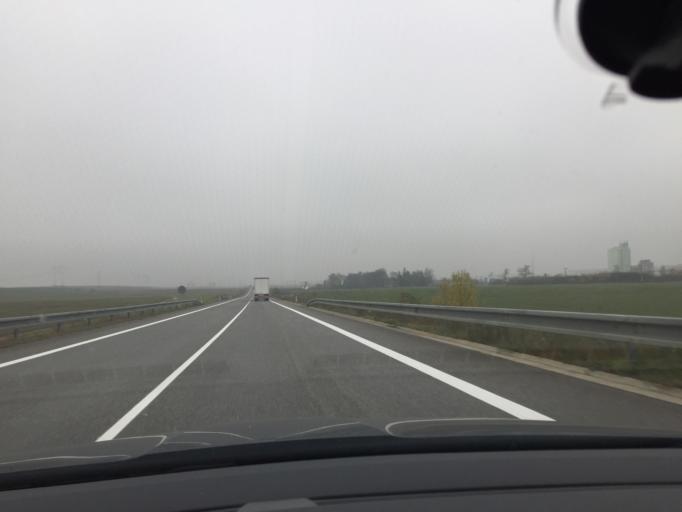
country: HU
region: Borsod-Abauj-Zemplen
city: Putnok
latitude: 48.4288
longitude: 20.3397
